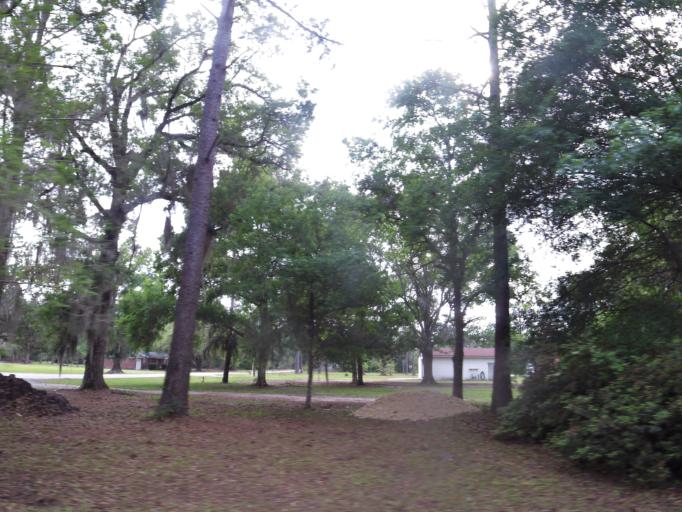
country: US
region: Florida
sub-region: Nassau County
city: Hilliard
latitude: 30.6882
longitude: -81.9207
